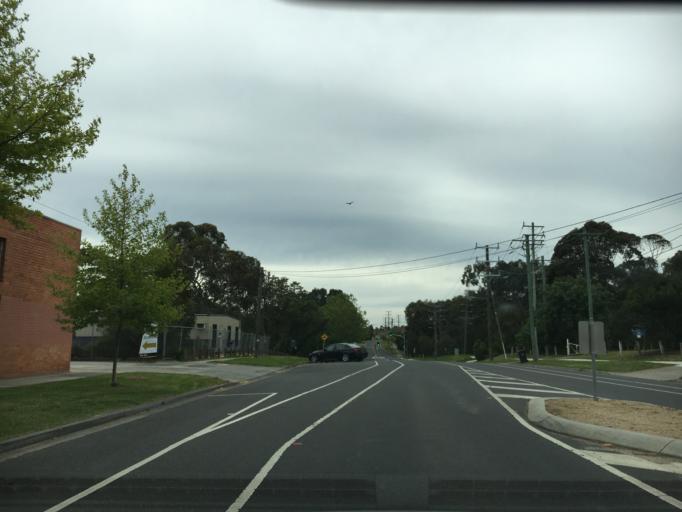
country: AU
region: Victoria
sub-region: Monash
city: Chadstone
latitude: -37.8920
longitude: 145.0936
